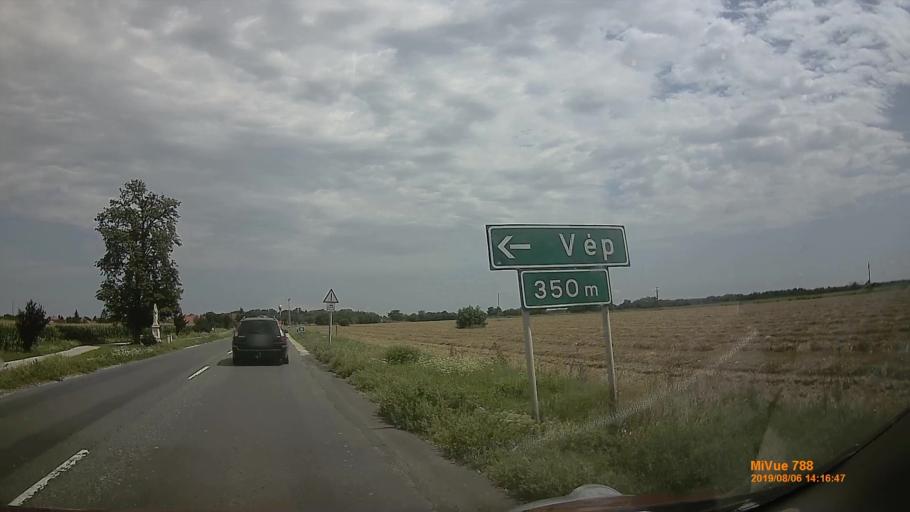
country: HU
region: Vas
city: Taplanszentkereszt
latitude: 47.1895
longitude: 16.7245
